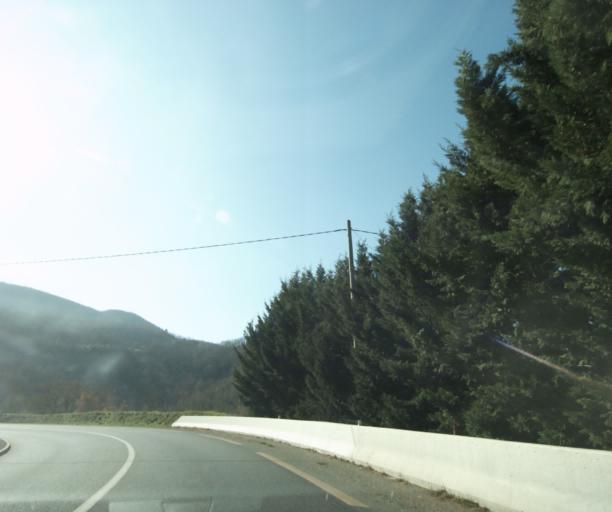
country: FR
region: Midi-Pyrenees
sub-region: Departement de l'Aveyron
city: Saint-Affrique
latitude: 43.9469
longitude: 2.9036
